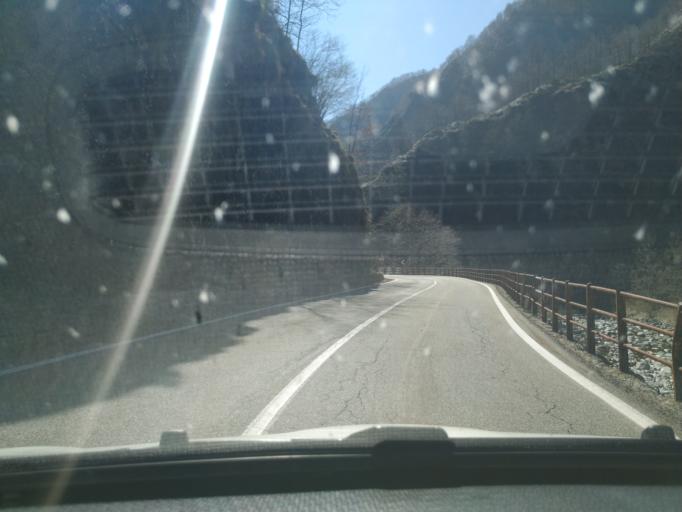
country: IT
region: Piedmont
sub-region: Provincia di Vercelli
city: Cervatto
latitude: 45.8731
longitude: 8.1849
